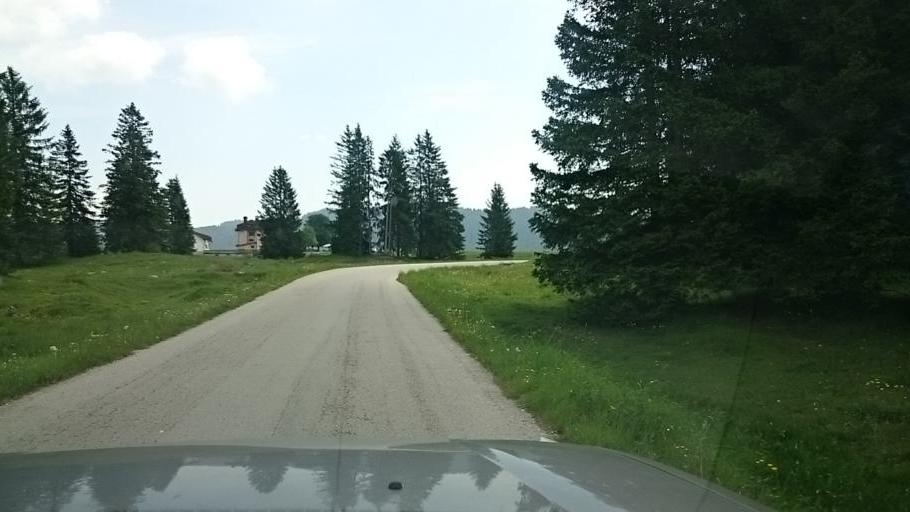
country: IT
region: Trentino-Alto Adige
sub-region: Provincia di Trento
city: Grigno
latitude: 45.9640
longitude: 11.6007
